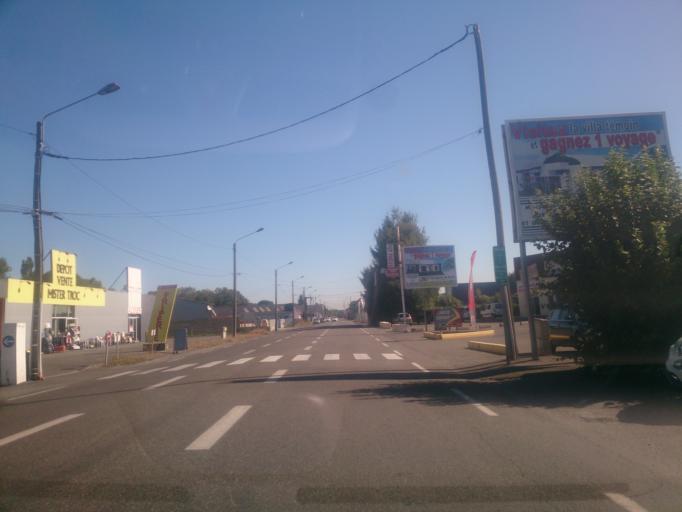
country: FR
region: Midi-Pyrenees
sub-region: Departement des Hautes-Pyrenees
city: Juillan
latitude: 43.1944
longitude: 0.0275
